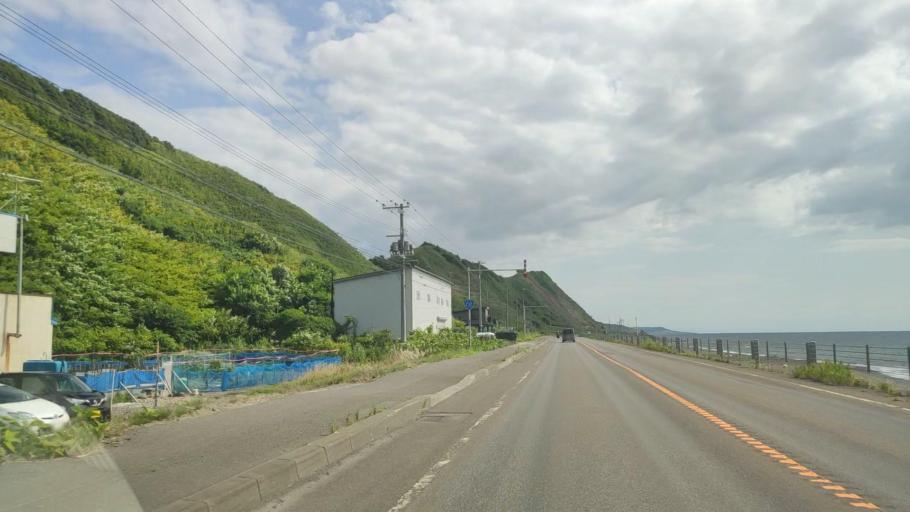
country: JP
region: Hokkaido
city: Rumoi
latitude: 44.2179
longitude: 141.6559
